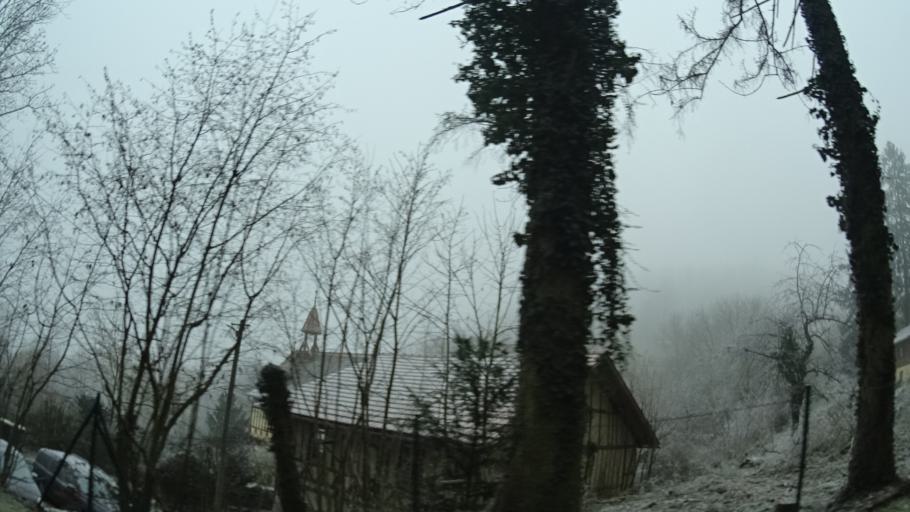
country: DE
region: Bavaria
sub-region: Regierungsbezirk Unterfranken
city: Zeil
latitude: 50.0809
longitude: 10.5752
